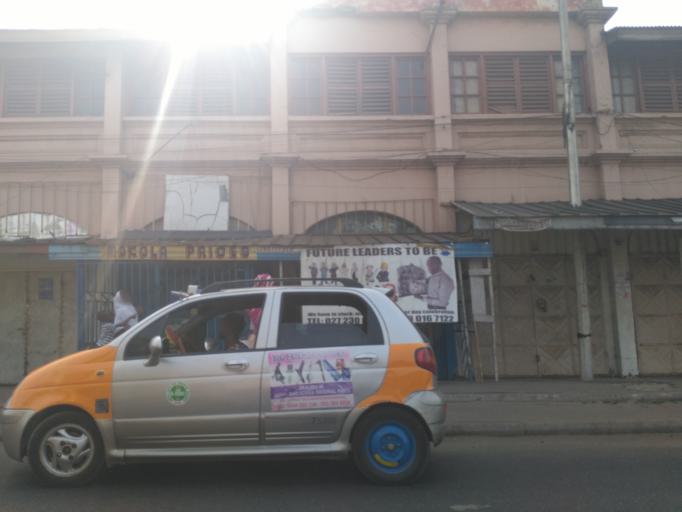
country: GH
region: Greater Accra
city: Accra
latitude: 5.5372
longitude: -0.2101
